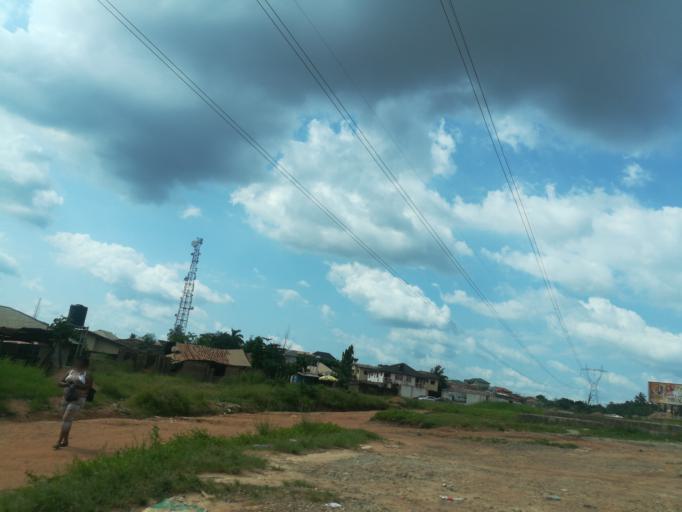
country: NG
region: Oyo
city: Ibadan
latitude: 7.4202
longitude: 3.8472
